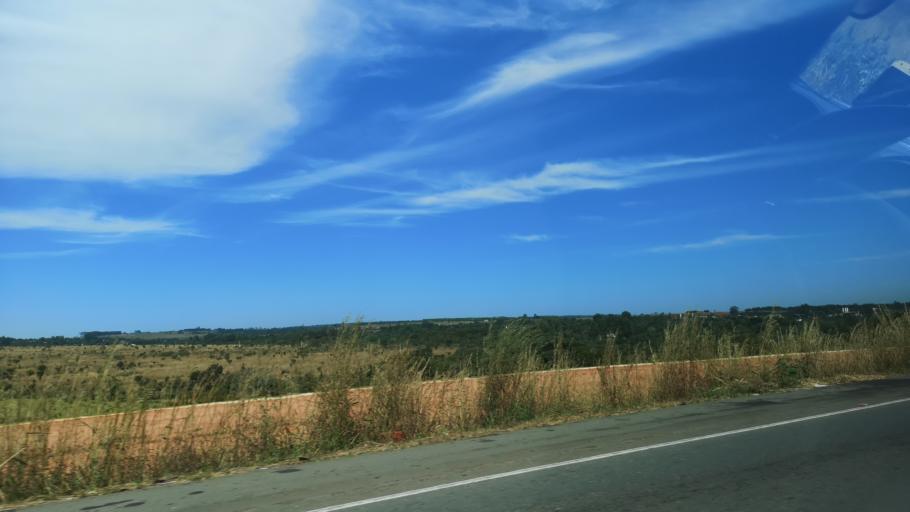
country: BR
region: Goias
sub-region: Senador Canedo
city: Senador Canedo
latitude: -16.7368
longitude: -49.1199
